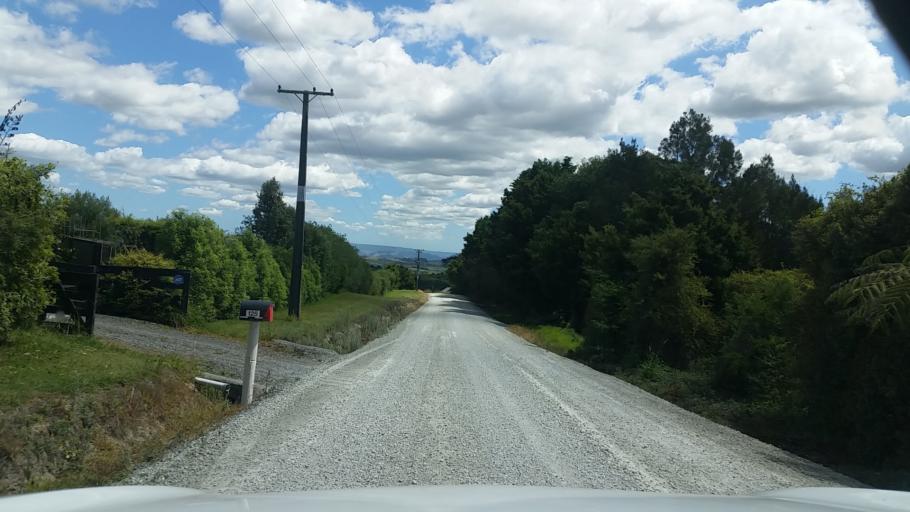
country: NZ
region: Northland
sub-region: Whangarei
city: Maungatapere
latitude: -35.6679
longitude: 174.1728
